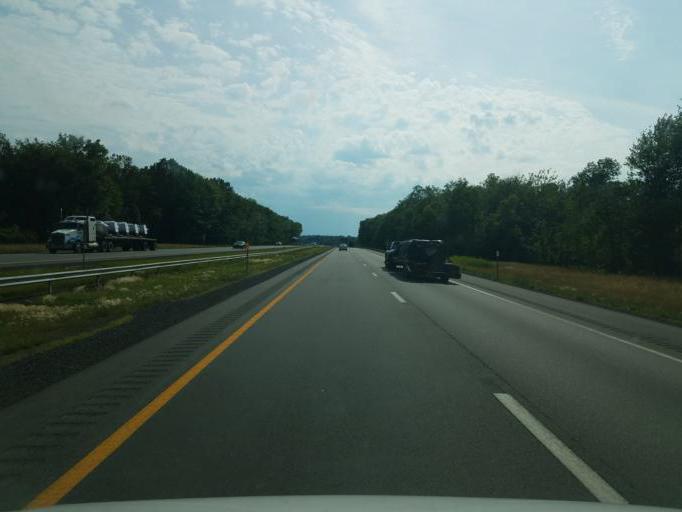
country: US
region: New York
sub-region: Chautauqua County
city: Silver Creek
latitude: 42.5006
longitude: -79.2282
